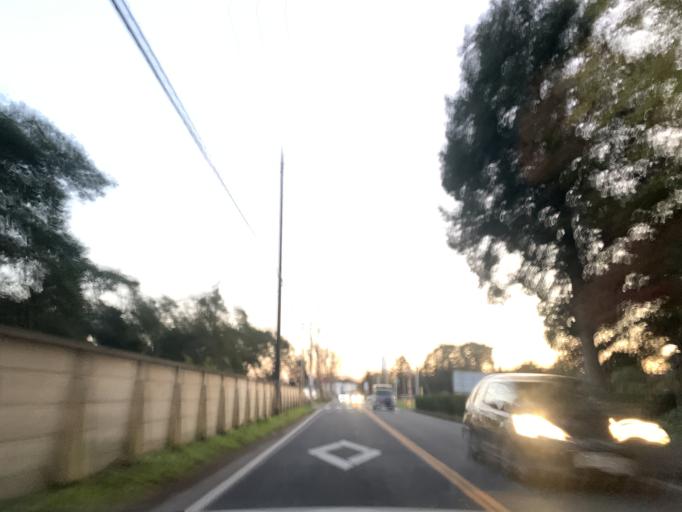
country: JP
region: Chiba
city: Nagareyama
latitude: 35.8884
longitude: 139.9014
